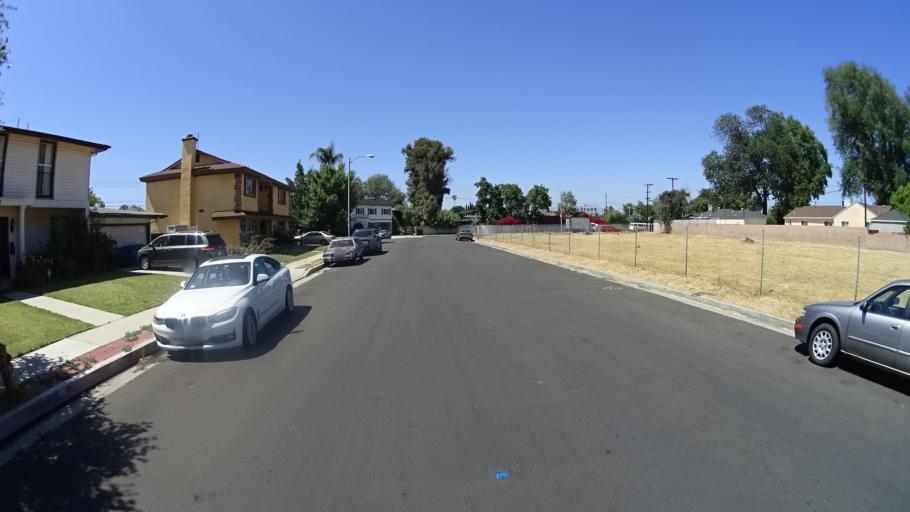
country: US
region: California
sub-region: Los Angeles County
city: Van Nuys
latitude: 34.1924
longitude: -118.4969
